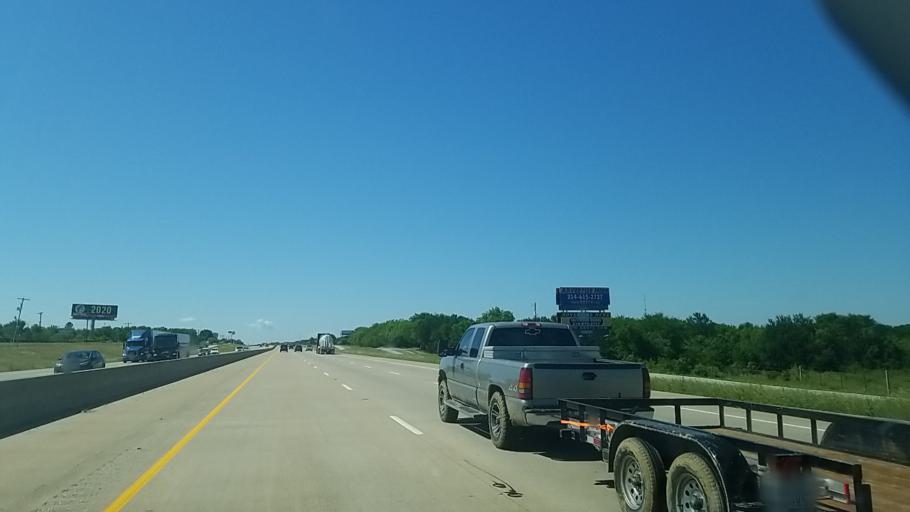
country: US
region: Texas
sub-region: Navarro County
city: Corsicana
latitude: 32.2344
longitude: -96.4913
